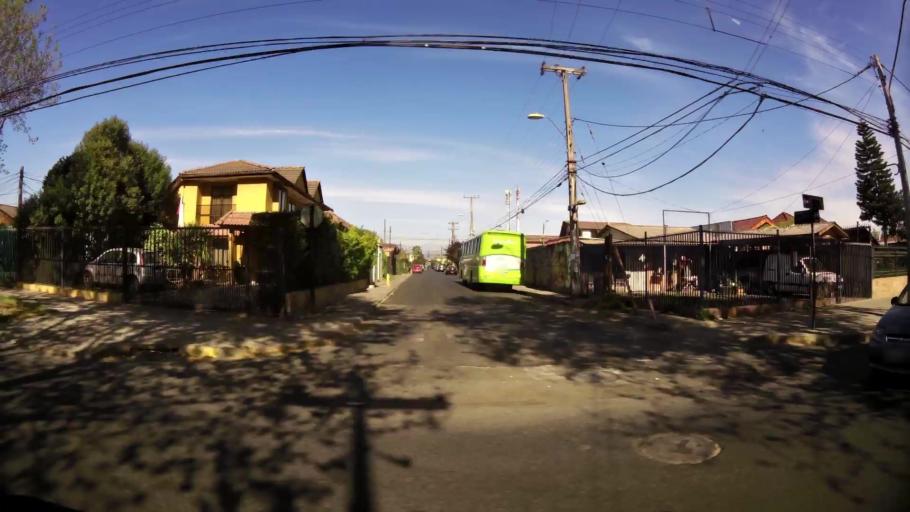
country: CL
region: Santiago Metropolitan
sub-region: Provincia de Santiago
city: Lo Prado
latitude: -33.4726
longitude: -70.7375
